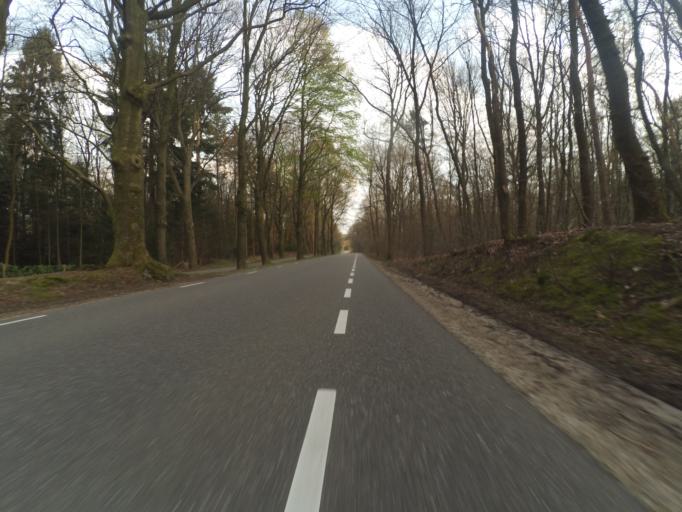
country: NL
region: Gelderland
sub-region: Gemeente Apeldoorn
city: Beekbergen
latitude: 52.1267
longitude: 5.8882
